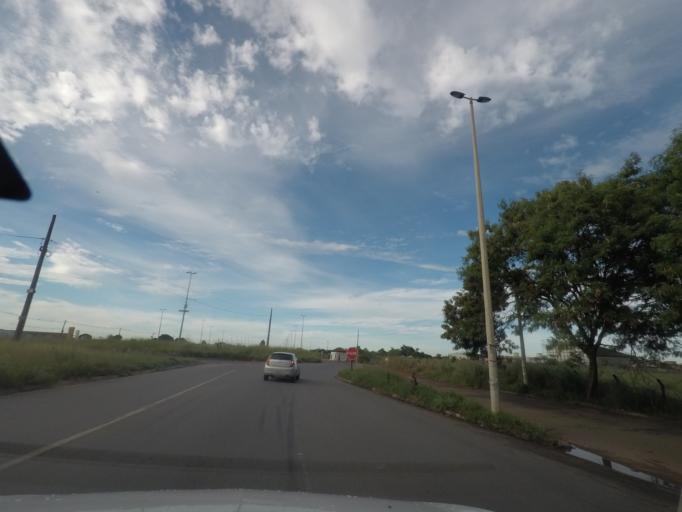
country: BR
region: Goias
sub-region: Aparecida De Goiania
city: Aparecida de Goiania
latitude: -16.7726
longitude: -49.3518
